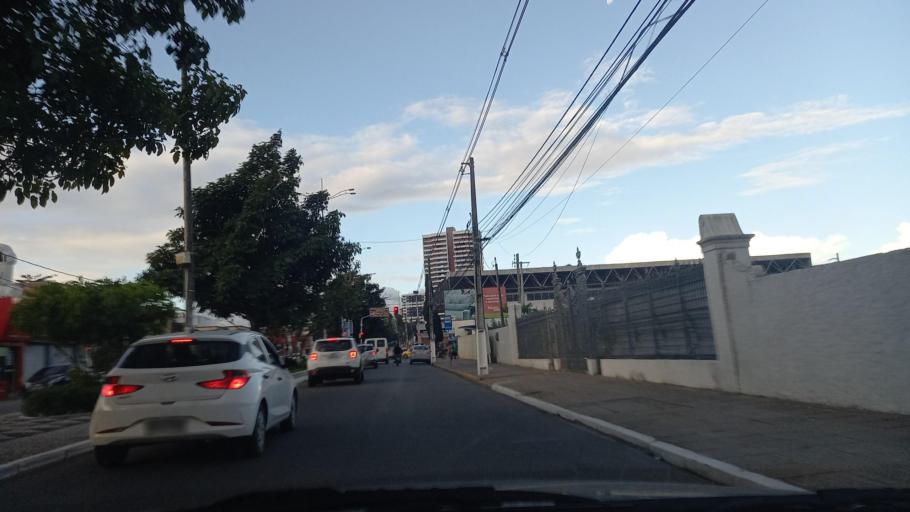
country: BR
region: Pernambuco
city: Garanhuns
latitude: -8.8835
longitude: -36.4799
